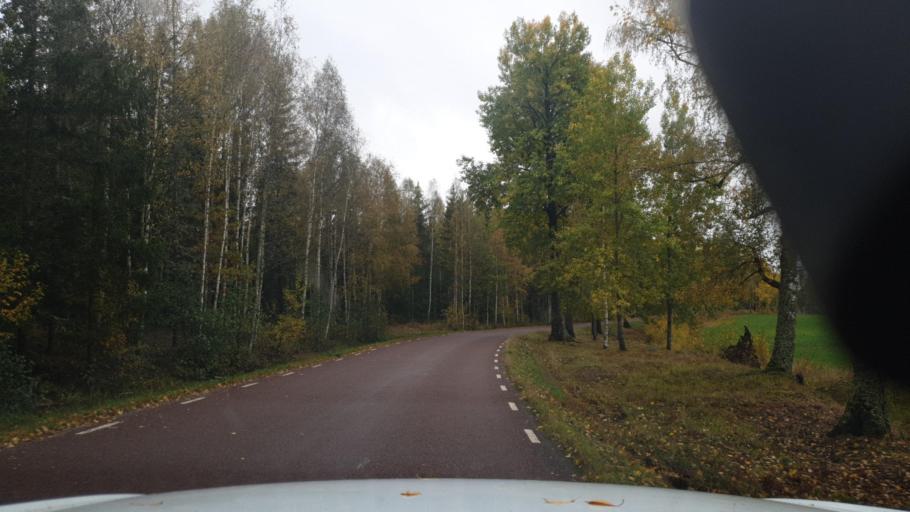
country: SE
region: Vaermland
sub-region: Karlstads Kommun
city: Valberg
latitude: 59.4411
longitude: 13.0905
